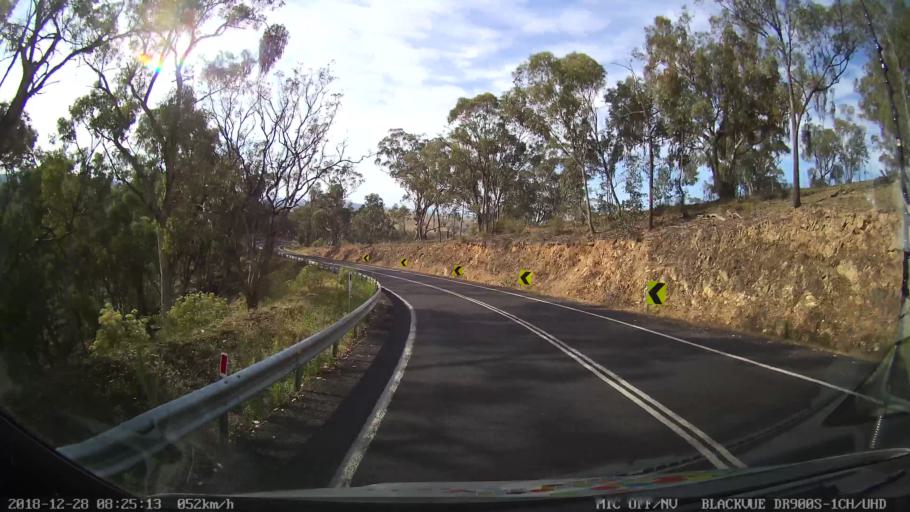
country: AU
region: New South Wales
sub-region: Blayney
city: Blayney
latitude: -33.9247
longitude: 149.3516
